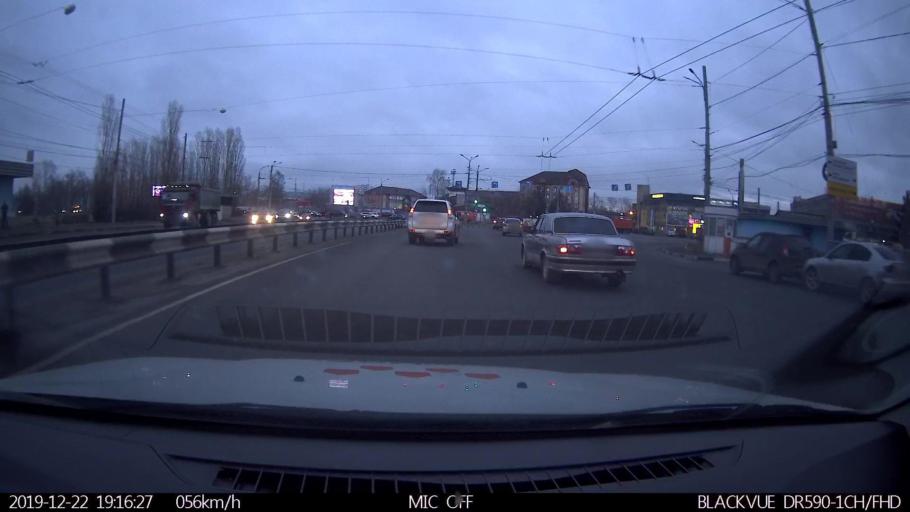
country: RU
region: Nizjnij Novgorod
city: Nizhniy Novgorod
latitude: 56.3202
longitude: 43.9275
